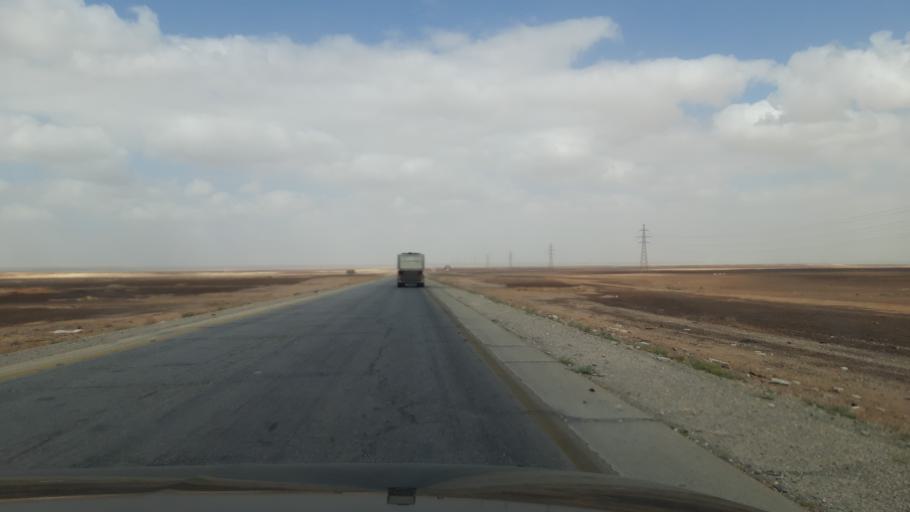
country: JO
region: Amman
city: Al Azraq ash Shamali
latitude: 31.7716
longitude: 36.5643
